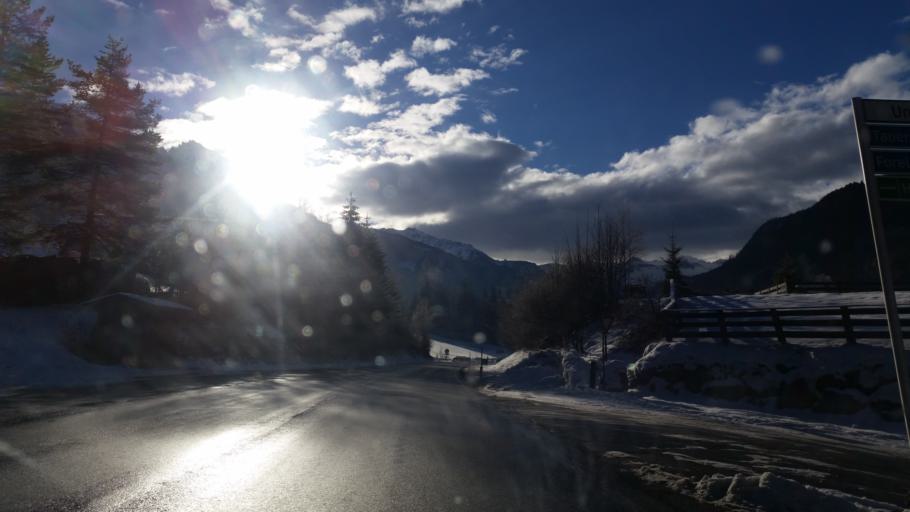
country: AT
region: Salzburg
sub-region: Politischer Bezirk Sankt Johann im Pongau
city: Forstau
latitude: 47.3424
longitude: 13.5040
